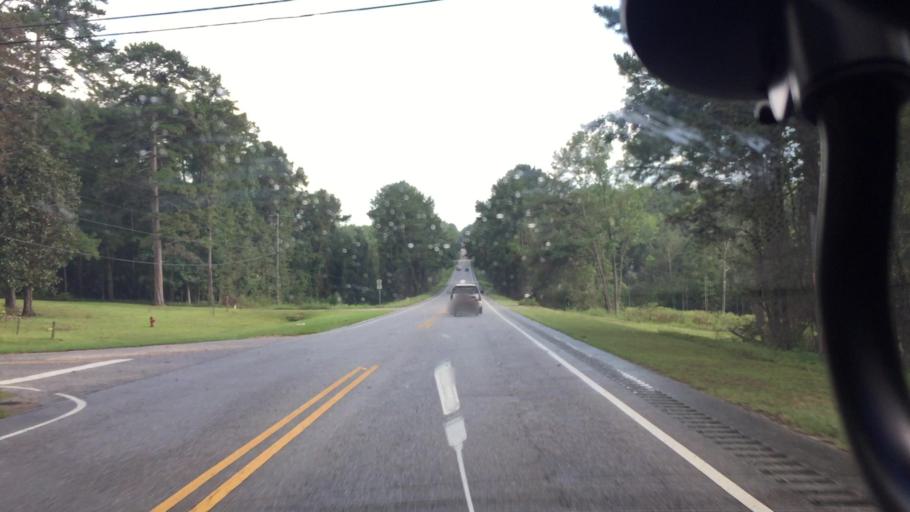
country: US
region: Alabama
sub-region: Coffee County
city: New Brockton
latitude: 31.4074
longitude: -85.8825
